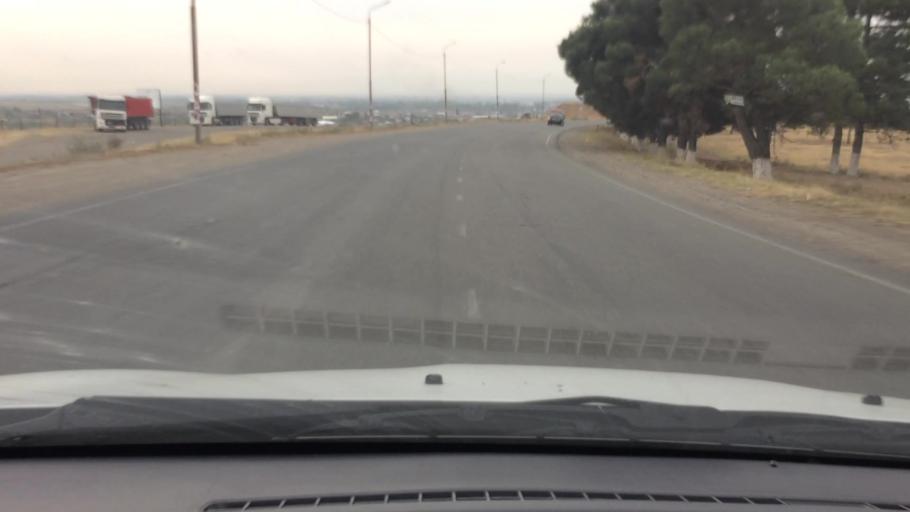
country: GE
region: Kvemo Kartli
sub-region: Marneuli
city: Marneuli
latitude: 41.5015
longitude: 44.8035
